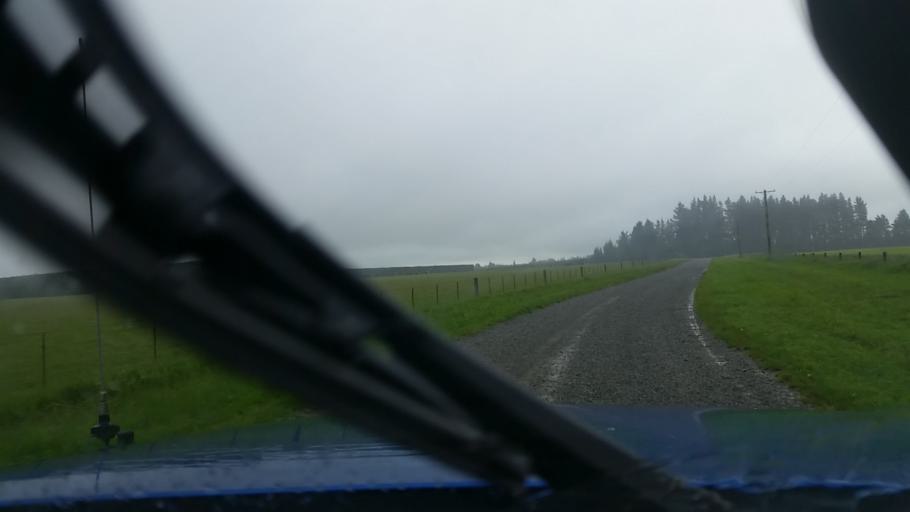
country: NZ
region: Canterbury
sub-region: Ashburton District
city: Methven
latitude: -43.7543
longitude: 171.2586
